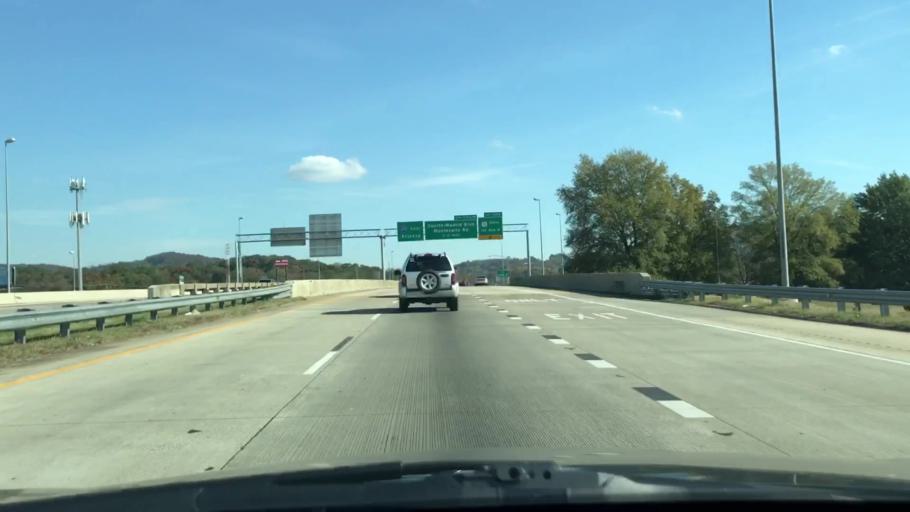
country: US
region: Alabama
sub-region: Jefferson County
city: Irondale
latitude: 33.5466
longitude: -86.7455
